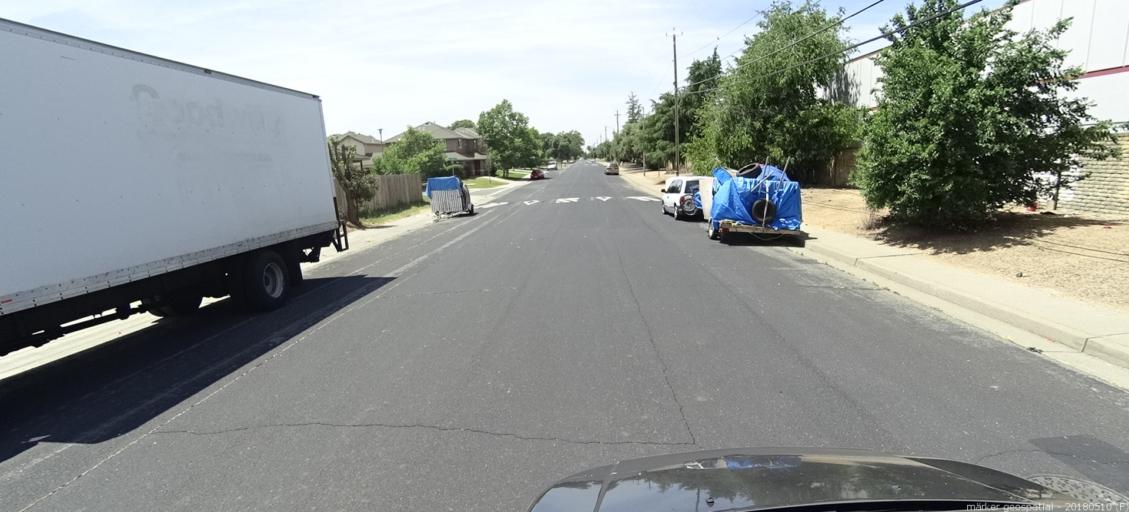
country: US
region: California
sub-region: Sacramento County
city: Rio Linda
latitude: 38.6378
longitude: -121.4603
